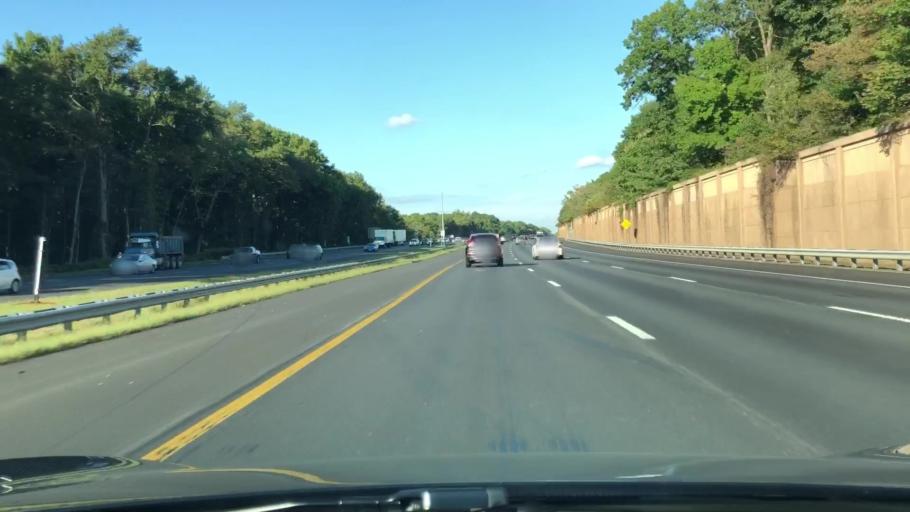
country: US
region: New Jersey
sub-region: Camden County
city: Kingston Estates
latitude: 39.9264
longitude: -74.9753
